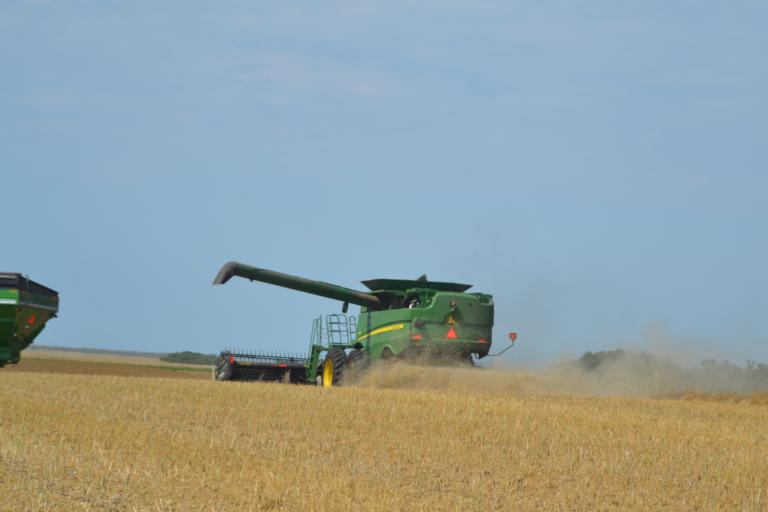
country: US
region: North Dakota
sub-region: Mercer County
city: Beulah
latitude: 47.6982
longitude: -101.9673
